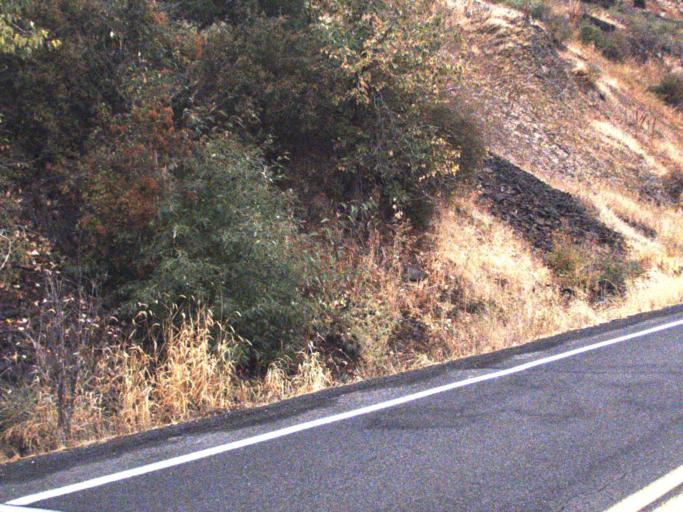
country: US
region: Washington
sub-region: Spokane County
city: Medical Lake
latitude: 47.7423
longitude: -117.8838
